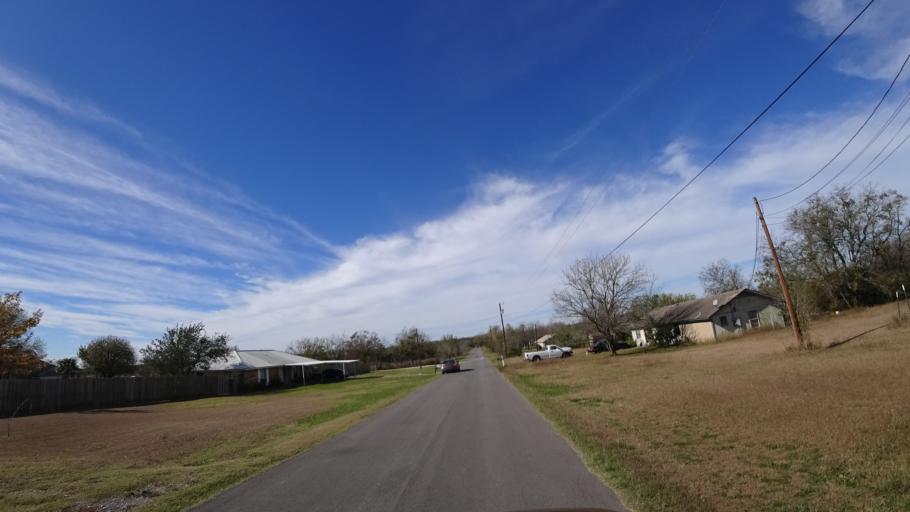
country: US
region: Texas
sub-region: Travis County
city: Onion Creek
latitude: 30.1049
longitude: -97.7193
